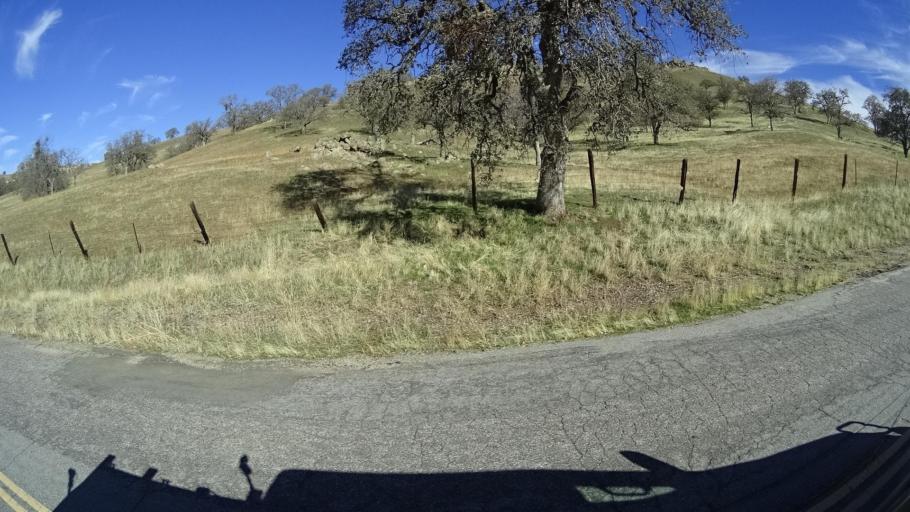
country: US
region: California
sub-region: Kern County
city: Alta Sierra
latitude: 35.6301
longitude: -118.7987
